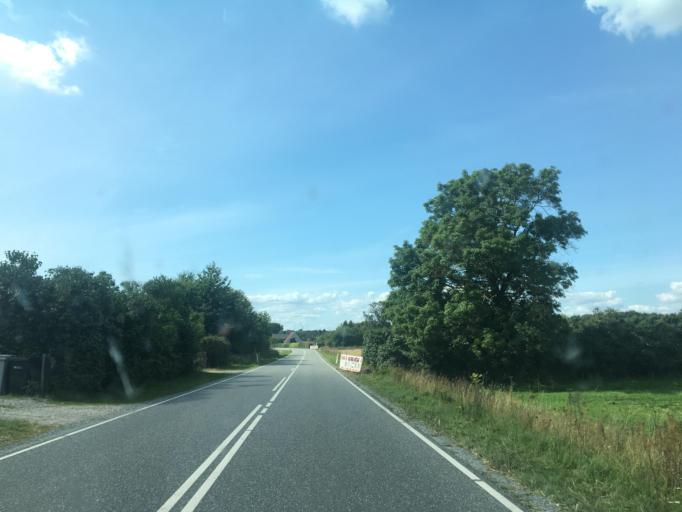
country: DK
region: South Denmark
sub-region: Middelfart Kommune
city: Ejby
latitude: 55.3924
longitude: 9.9458
